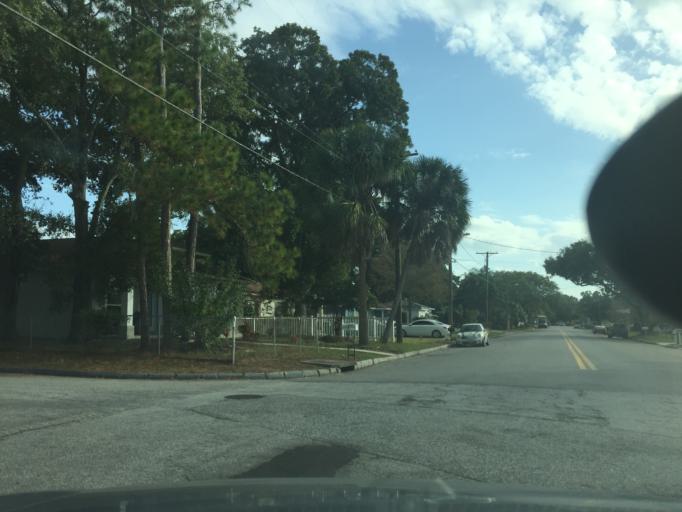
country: US
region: Florida
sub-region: Hillsborough County
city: Tampa
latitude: 27.9473
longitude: -82.4974
